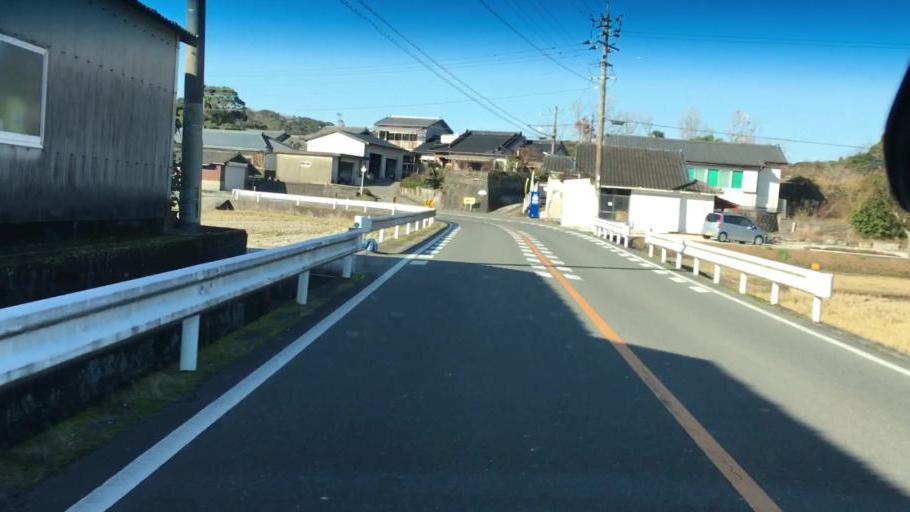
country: JP
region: Kagoshima
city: Satsumasendai
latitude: 31.8296
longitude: 130.2460
